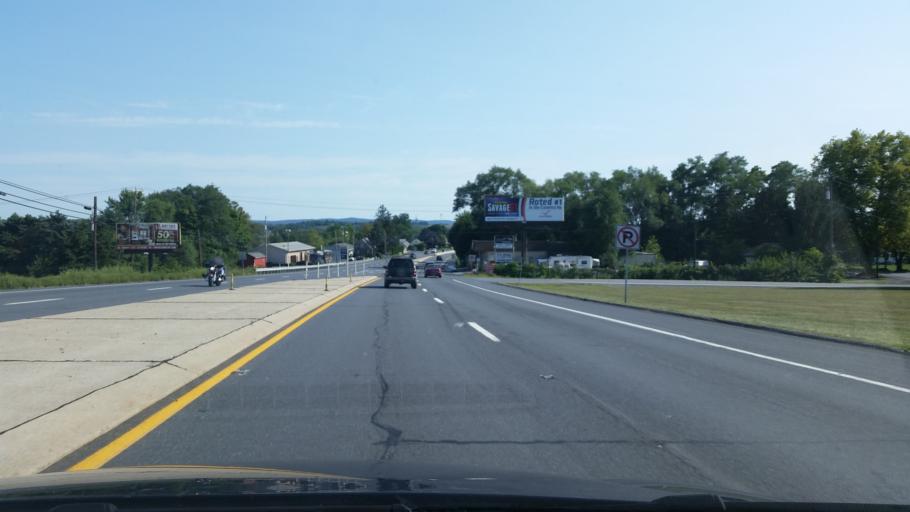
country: US
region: Pennsylvania
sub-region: Berks County
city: Shoemakersville
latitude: 40.5215
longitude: -75.9706
